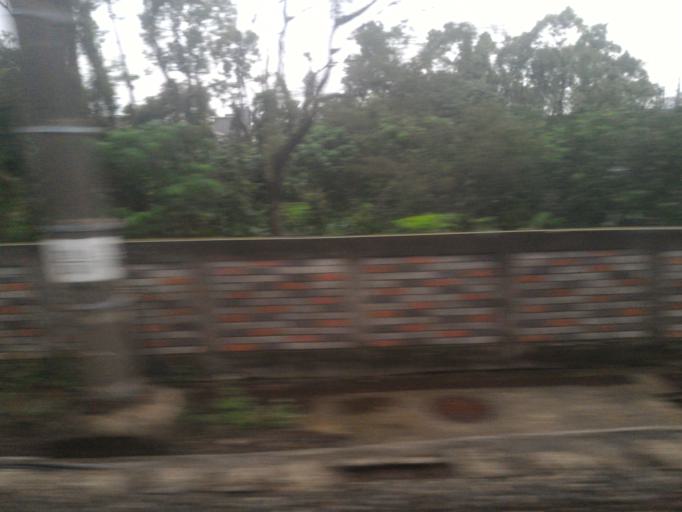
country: TW
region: Taipei
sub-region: Taipei
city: Banqiao
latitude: 25.0019
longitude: 121.4303
